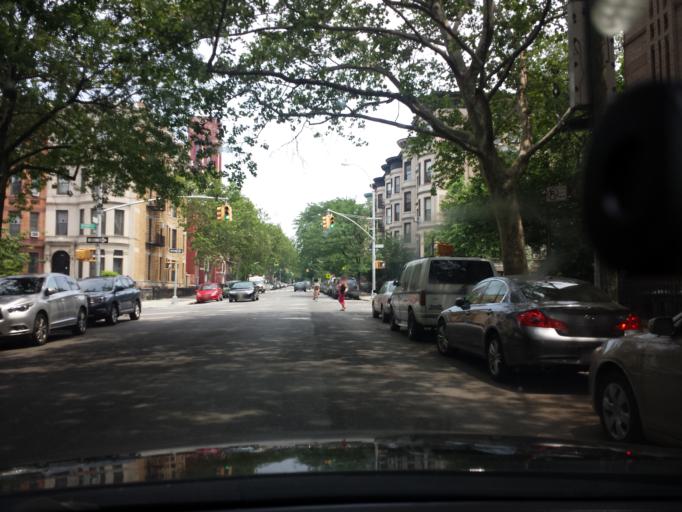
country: US
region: New York
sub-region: Kings County
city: Brooklyn
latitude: 40.6714
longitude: -73.9811
